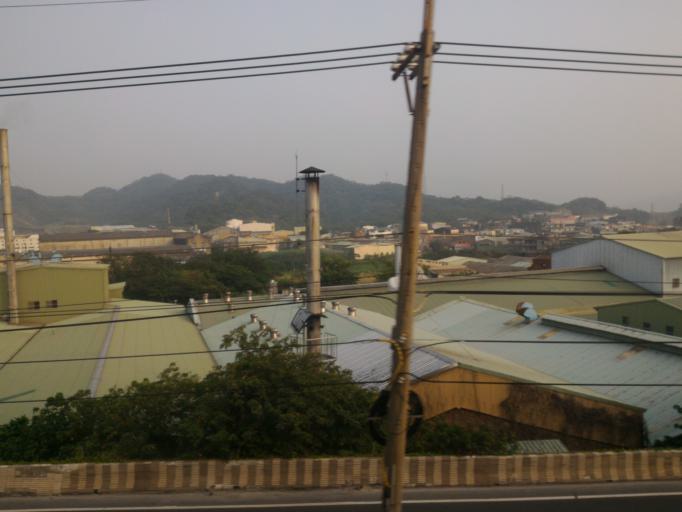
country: TW
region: Taiwan
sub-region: Taoyuan
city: Taoyuan
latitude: 24.9668
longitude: 121.3387
